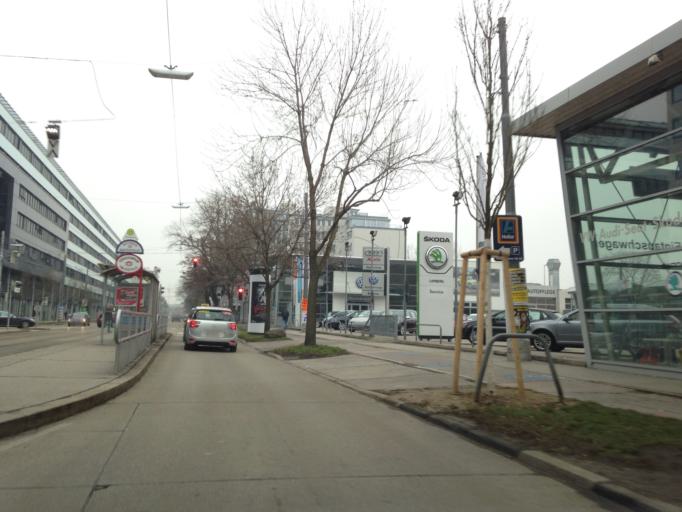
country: AT
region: Vienna
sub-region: Wien Stadt
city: Vienna
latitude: 48.2340
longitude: 16.3829
